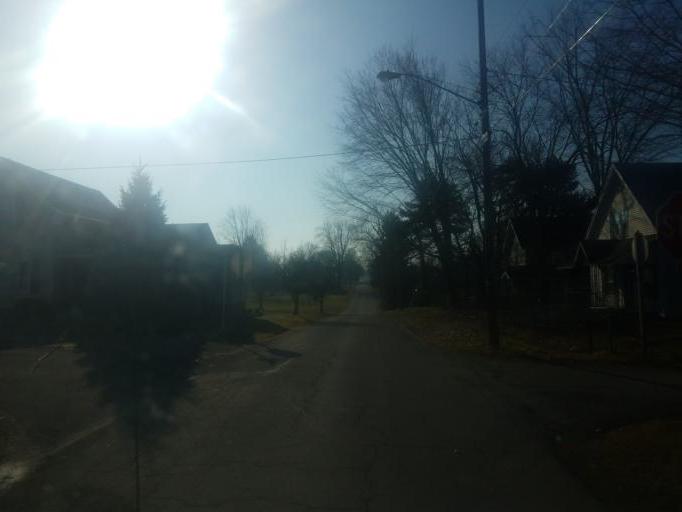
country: US
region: Ohio
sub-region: Seneca County
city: Tiffin
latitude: 41.0510
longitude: -83.0106
